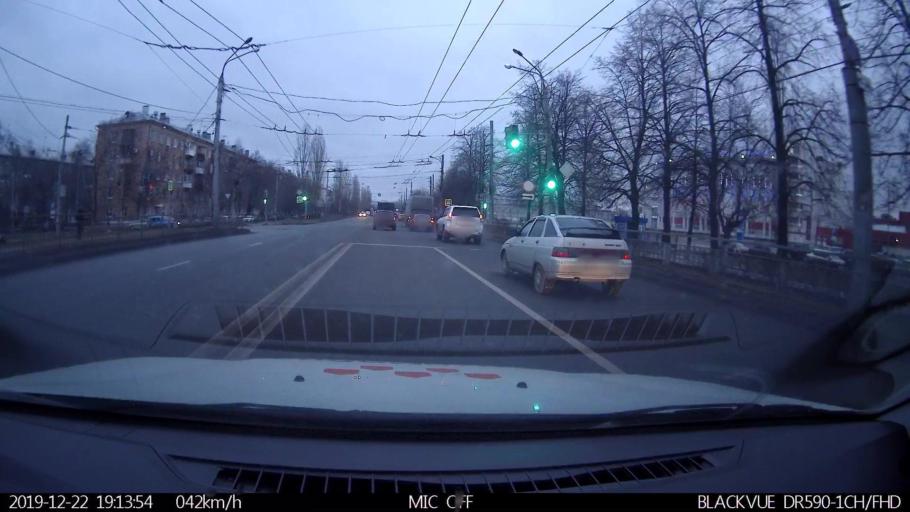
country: RU
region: Nizjnij Novgorod
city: Nizhniy Novgorod
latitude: 56.3284
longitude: 43.9062
